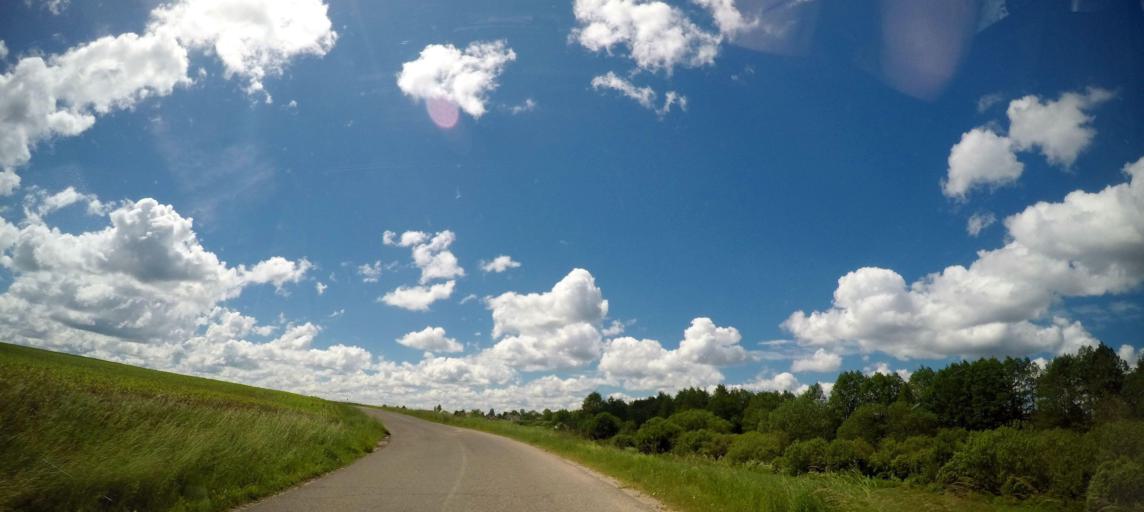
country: BY
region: Grodnenskaya
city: Hal'shany
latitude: 54.1718
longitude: 26.1000
